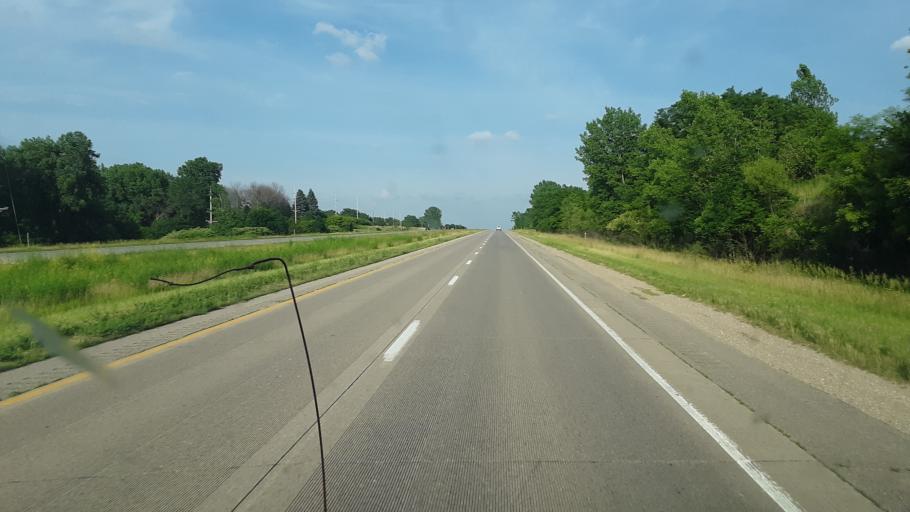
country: US
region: Iowa
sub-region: Marshall County
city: Marshalltown
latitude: 42.0061
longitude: -92.7452
